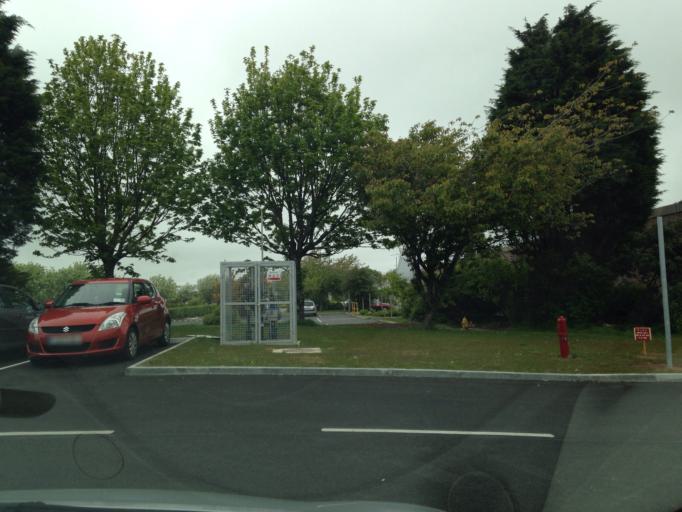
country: IE
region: Connaught
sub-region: County Galway
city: Gaillimh
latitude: 53.2927
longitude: -9.0064
